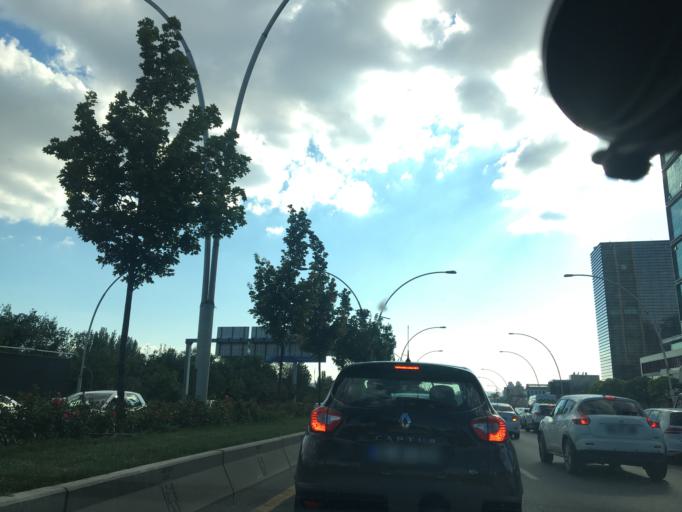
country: TR
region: Ankara
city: Ankara
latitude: 39.9094
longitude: 32.7997
